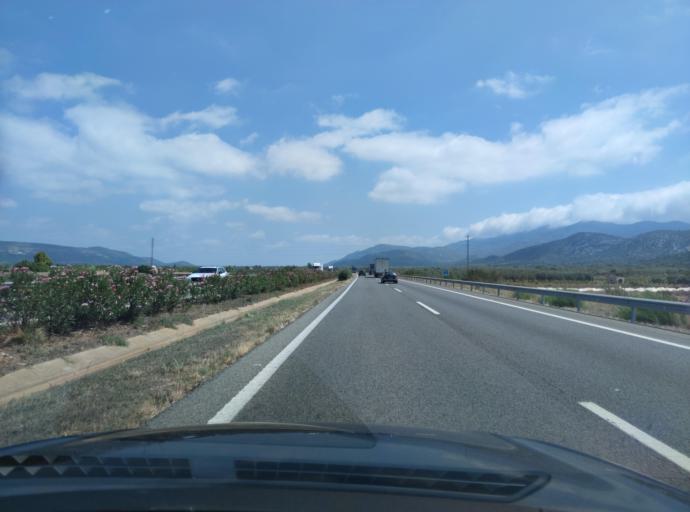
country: ES
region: Catalonia
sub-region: Provincia de Tarragona
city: Ulldecona
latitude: 40.5883
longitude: 0.4620
